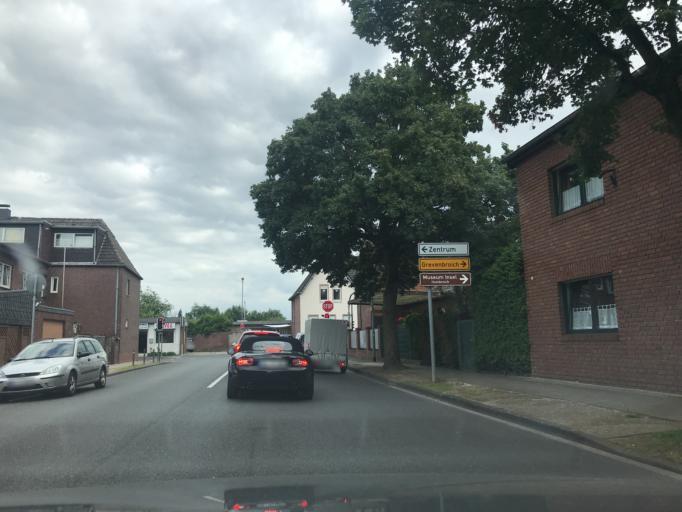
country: DE
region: North Rhine-Westphalia
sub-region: Regierungsbezirk Dusseldorf
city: Neuss
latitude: 51.1610
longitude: 6.6737
